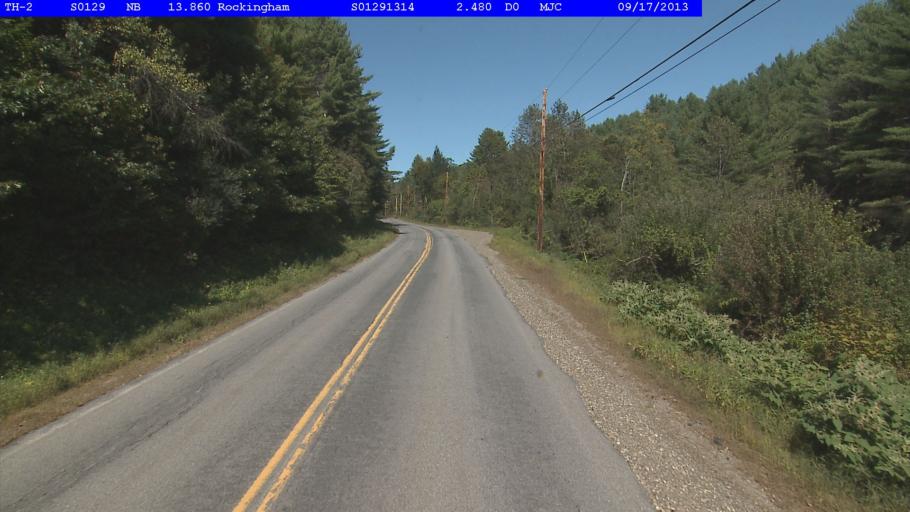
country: US
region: Vermont
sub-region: Windham County
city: Rockingham
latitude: 43.1531
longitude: -72.5177
